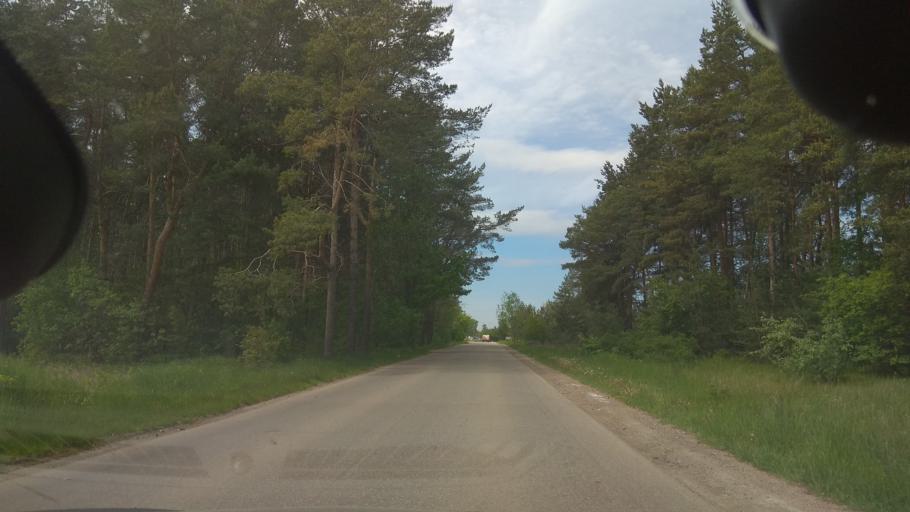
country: LT
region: Kauno apskritis
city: Jonava
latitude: 55.0888
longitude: 24.2923
